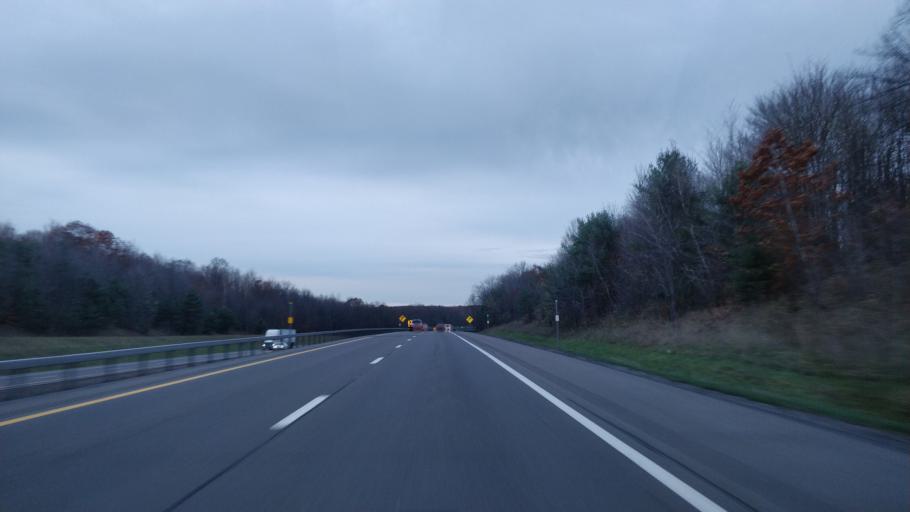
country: US
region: New York
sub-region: Oswego County
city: Central Square
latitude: 43.3695
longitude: -76.1214
